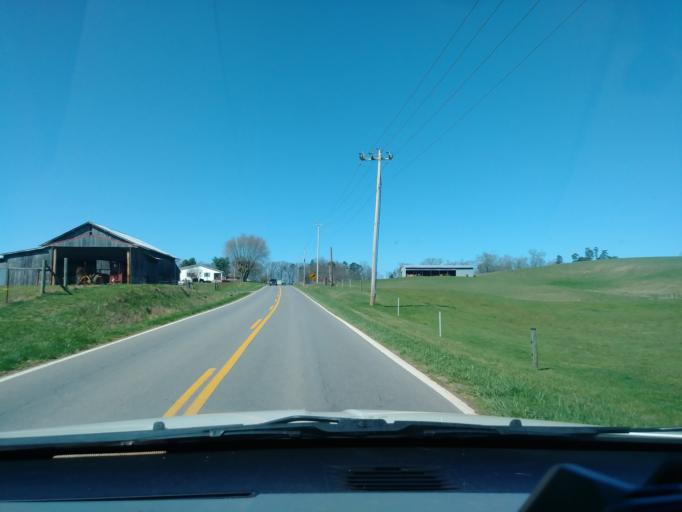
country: US
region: Tennessee
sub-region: Cocke County
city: Newport
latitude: 35.9914
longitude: -83.0683
